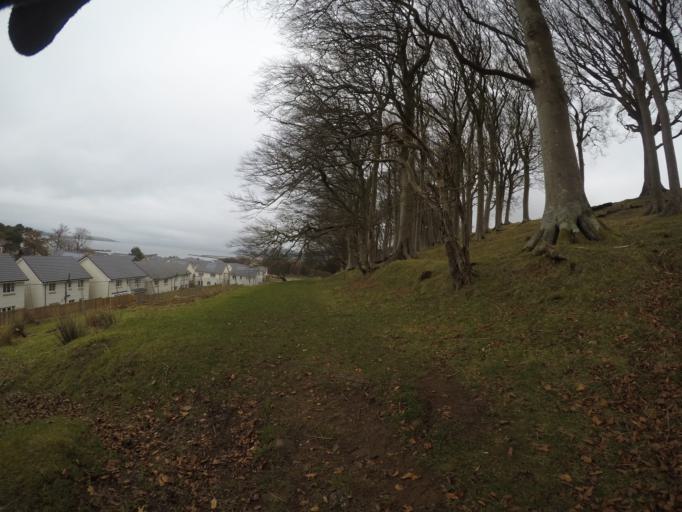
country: GB
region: Scotland
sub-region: North Ayrshire
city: Fairlie
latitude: 55.7593
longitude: -4.8497
